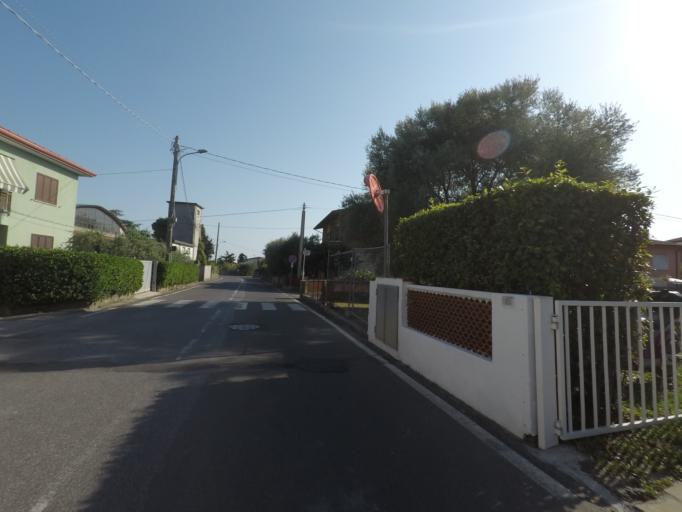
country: IT
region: Liguria
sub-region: Provincia di La Spezia
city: Casano-Dogana-Isola
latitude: 44.0647
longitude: 10.0309
